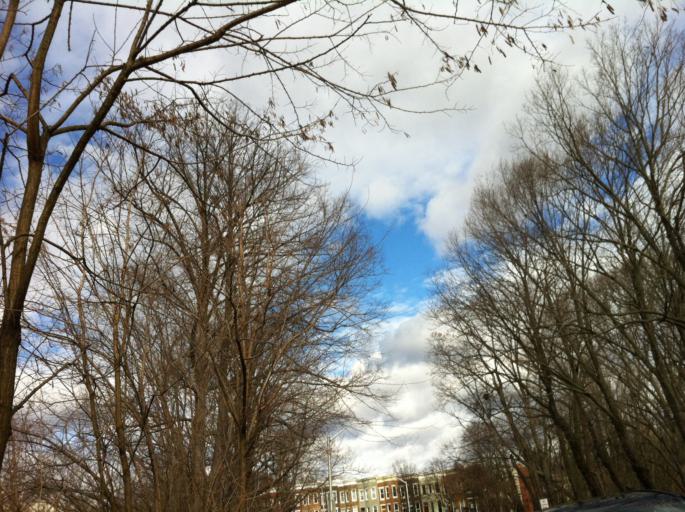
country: US
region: Maryland
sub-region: City of Baltimore
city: Baltimore
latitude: 39.3262
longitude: -76.6255
